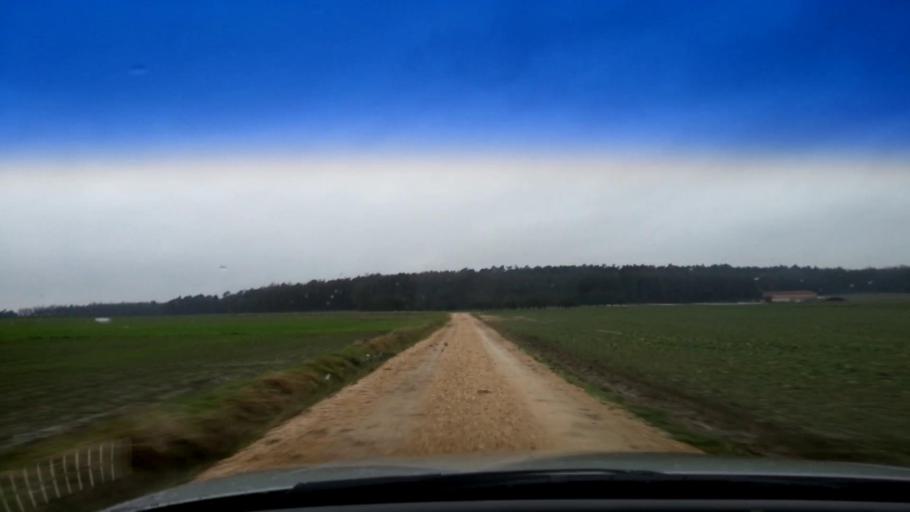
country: DE
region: Bavaria
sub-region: Upper Franconia
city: Memmelsdorf
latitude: 49.9609
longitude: 10.9471
